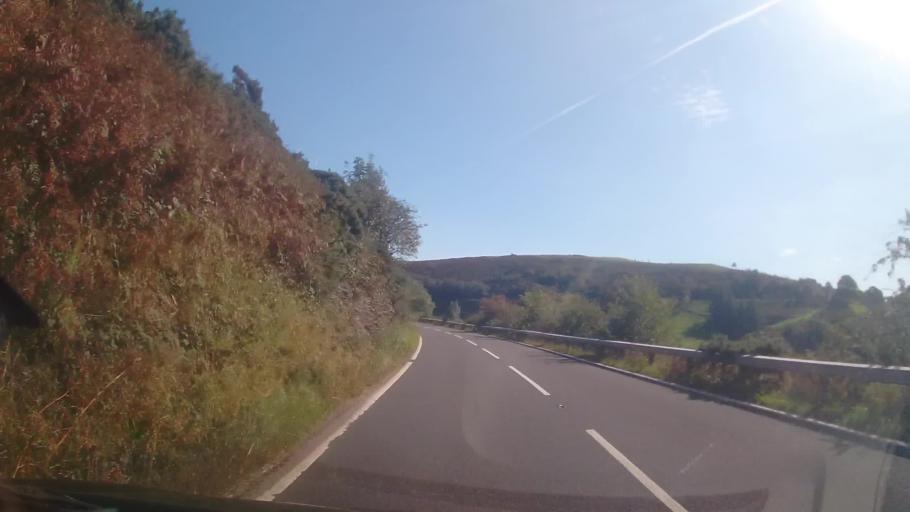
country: GB
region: Wales
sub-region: Sir Powys
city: Mochdre
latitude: 52.4546
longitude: -3.3469
